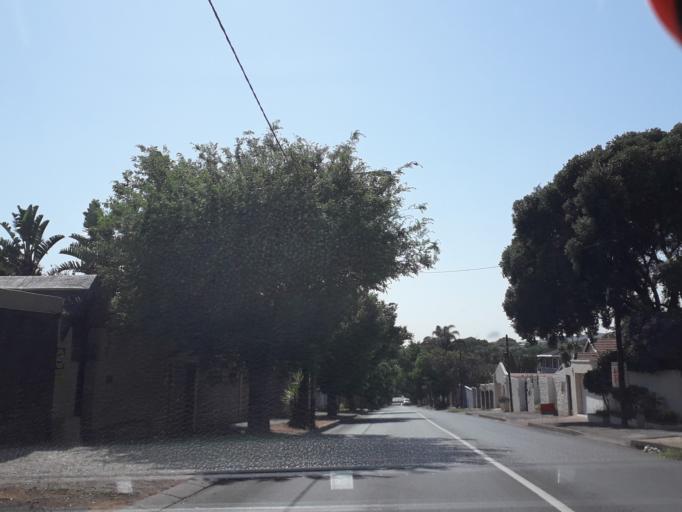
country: ZA
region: Gauteng
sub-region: City of Johannesburg Metropolitan Municipality
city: Johannesburg
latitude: -26.1558
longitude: 28.0664
